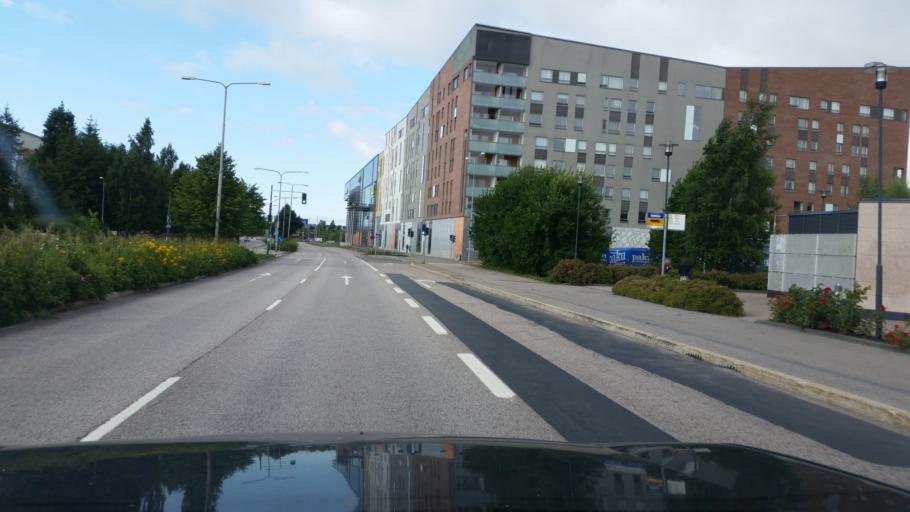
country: FI
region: Uusimaa
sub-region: Helsinki
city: Vantaa
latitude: 60.2147
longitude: 25.0921
